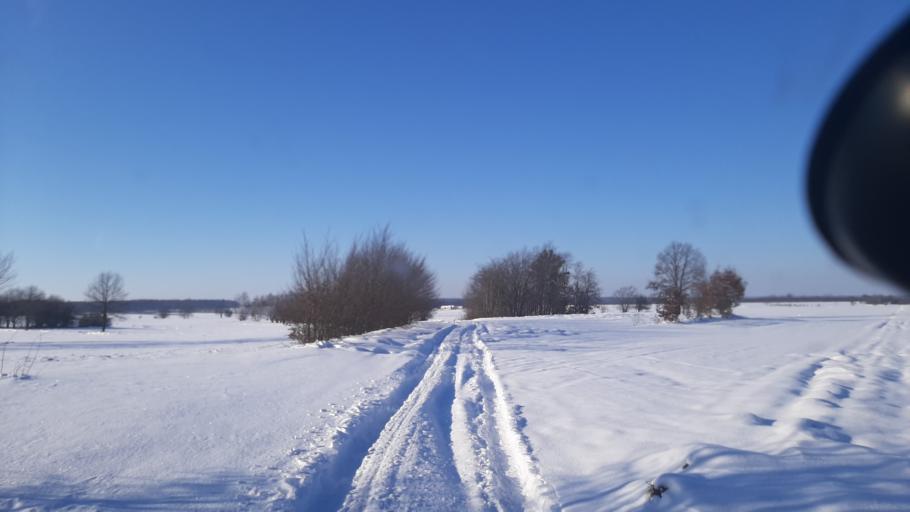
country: PL
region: Lublin Voivodeship
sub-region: Powiat lubelski
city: Jastkow
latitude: 51.3781
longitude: 22.4347
